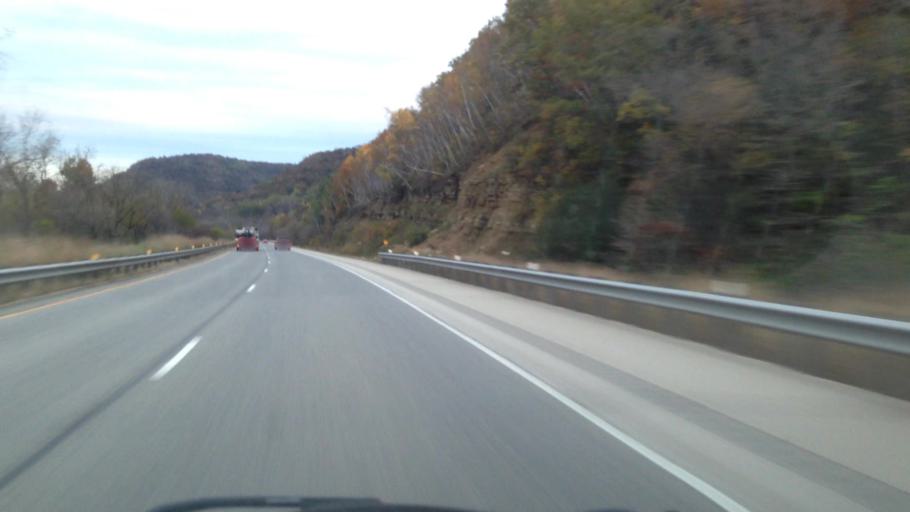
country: US
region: Wisconsin
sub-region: Trempealeau County
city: Trempealeau
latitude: 43.9273
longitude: -91.4107
